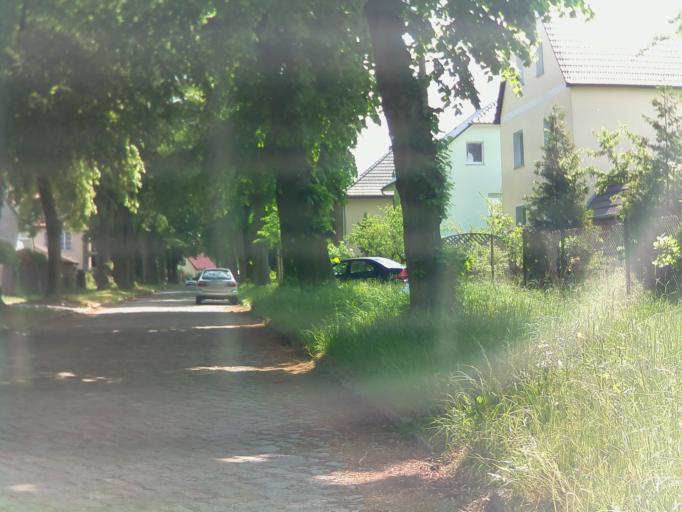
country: DE
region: Brandenburg
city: Dallgow-Doeberitz
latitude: 52.5578
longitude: 13.0695
